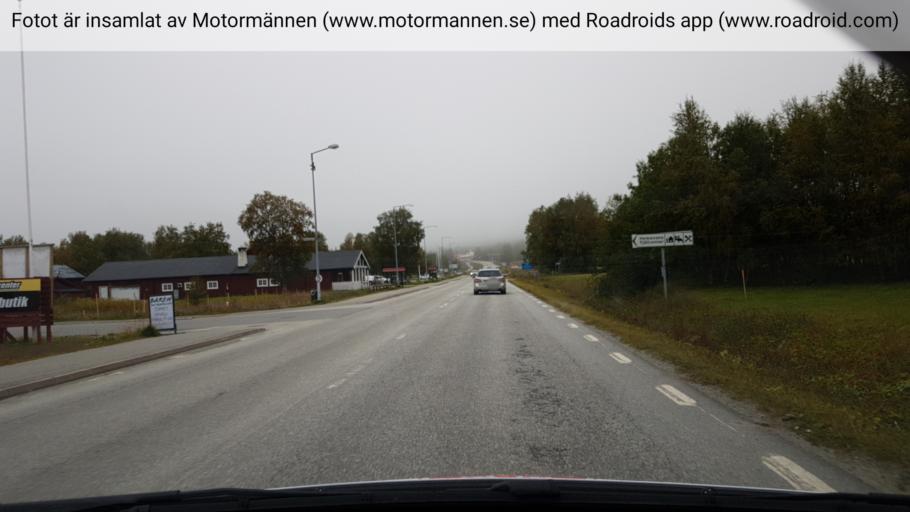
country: NO
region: Nordland
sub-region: Rana
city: Mo i Rana
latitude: 65.8121
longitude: 15.0883
